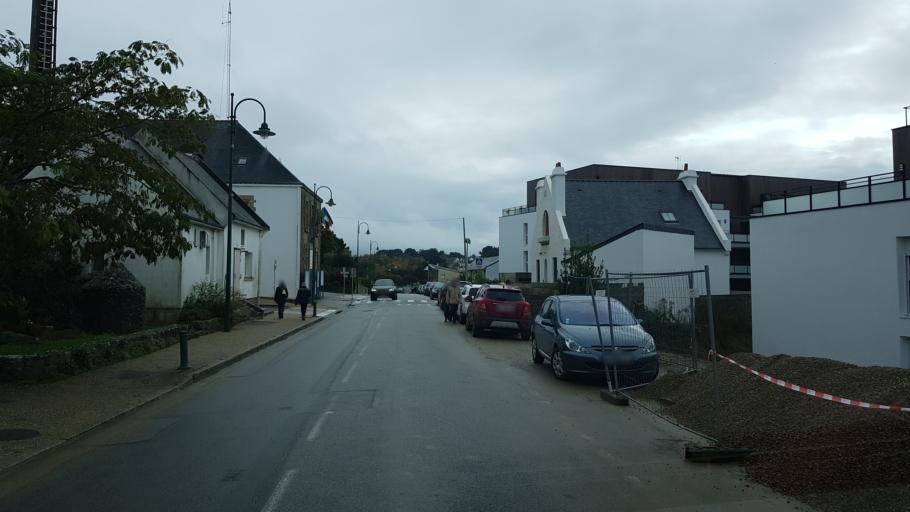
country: FR
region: Brittany
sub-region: Departement du Morbihan
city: Arzon
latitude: 47.5483
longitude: -2.8923
